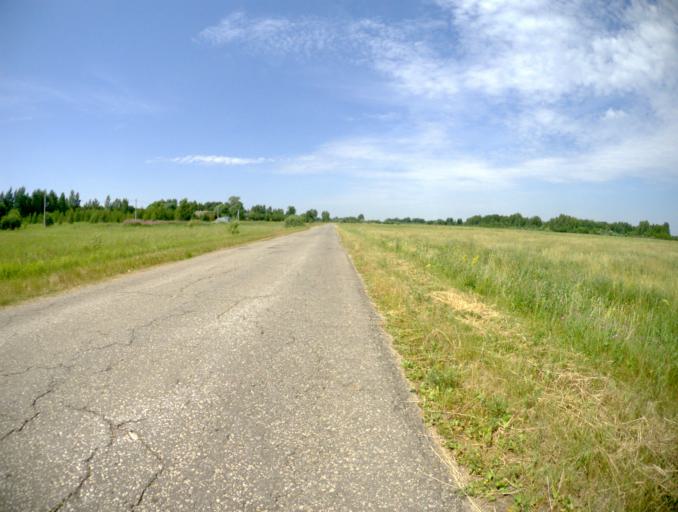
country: RU
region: Vladimir
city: Vorsha
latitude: 56.0232
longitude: 40.1967
